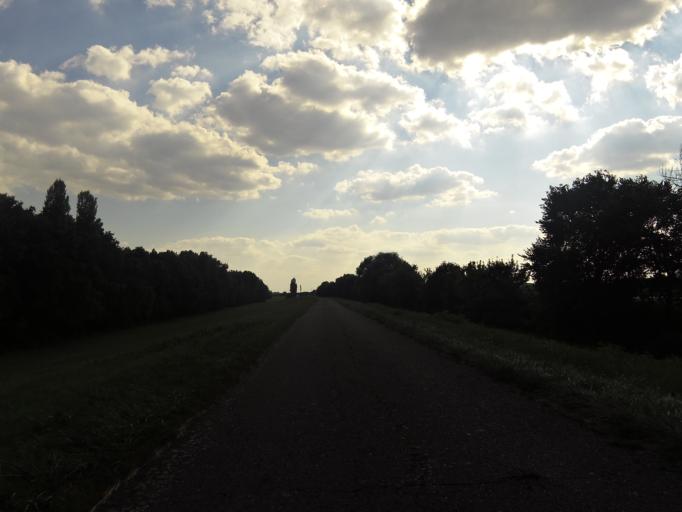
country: HU
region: Jasz-Nagykun-Szolnok
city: Abadszalok
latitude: 47.5341
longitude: 20.6215
